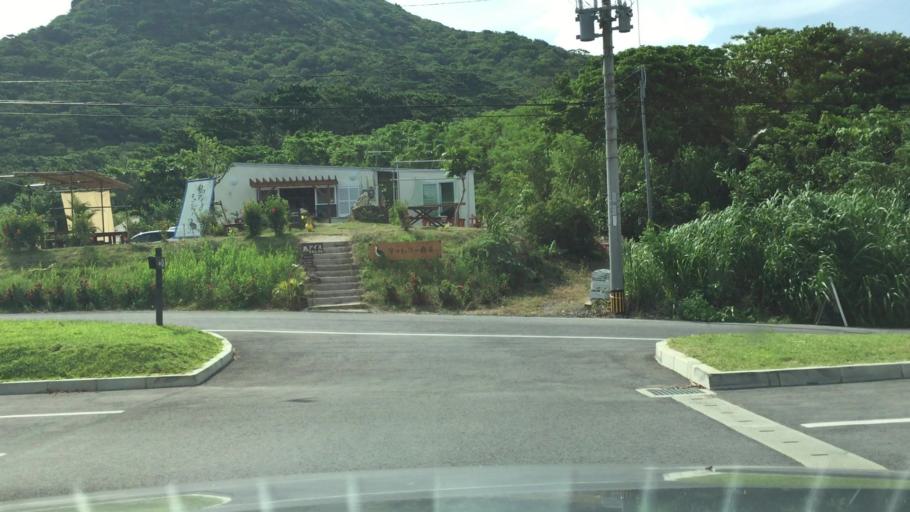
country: JP
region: Okinawa
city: Ishigaki
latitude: 24.4914
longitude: 124.2776
